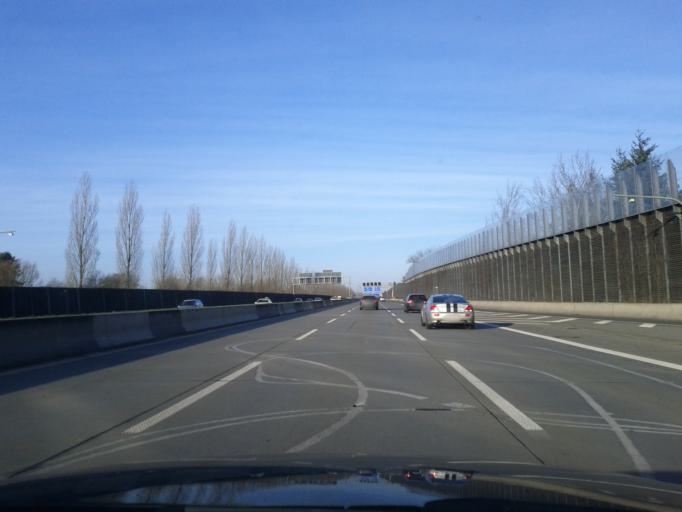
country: DE
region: Berlin
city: Buckow
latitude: 52.4439
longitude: 13.4771
